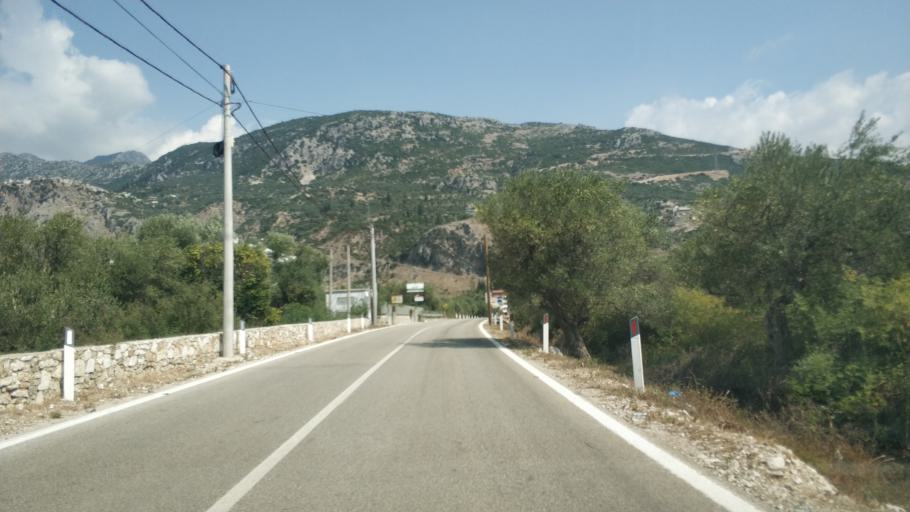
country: AL
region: Vlore
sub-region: Rrethi i Vlores
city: Himare
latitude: 40.0561
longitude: 19.8175
